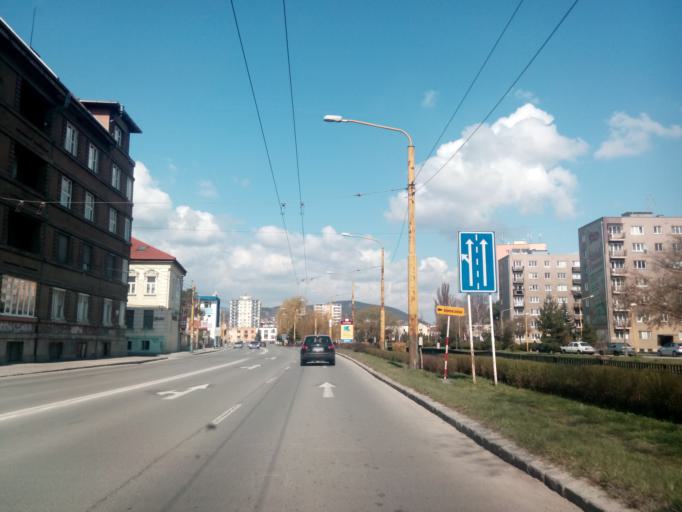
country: SK
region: Kosicky
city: Kosice
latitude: 48.7292
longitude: 21.2562
